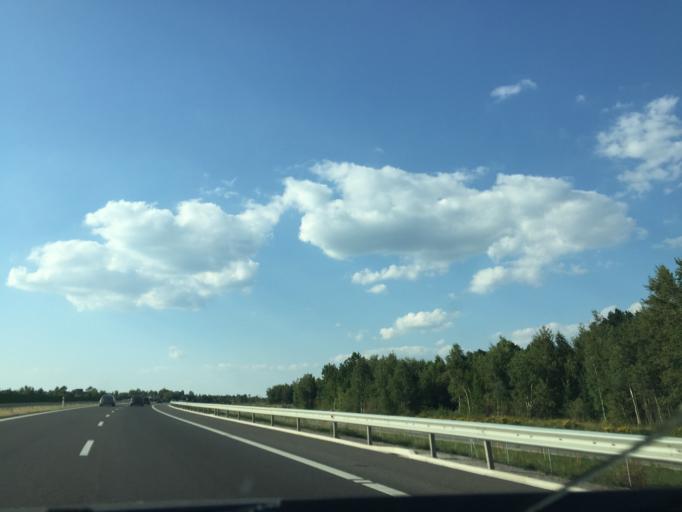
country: PL
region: Swietokrzyskie
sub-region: Powiat skarzyski
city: Skarzysko-Kamienna
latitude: 51.1336
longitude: 20.8342
